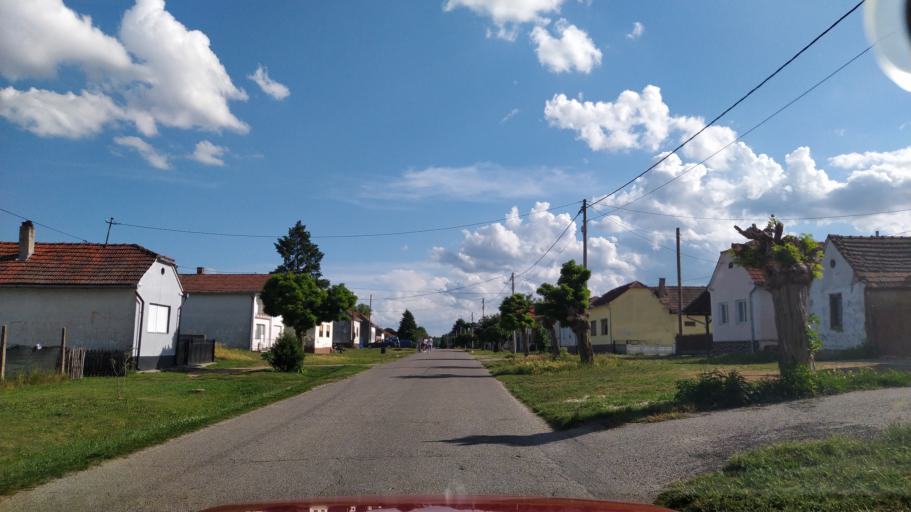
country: HR
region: Virovitick-Podravska
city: Pitomaca
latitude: 45.9615
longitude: 17.2153
